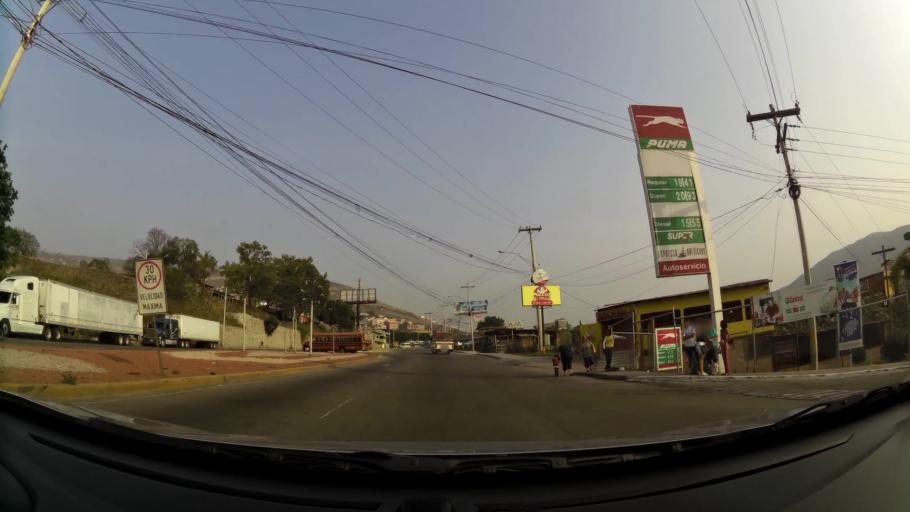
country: HN
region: Francisco Morazan
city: El Lolo
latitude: 14.1050
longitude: -87.2430
